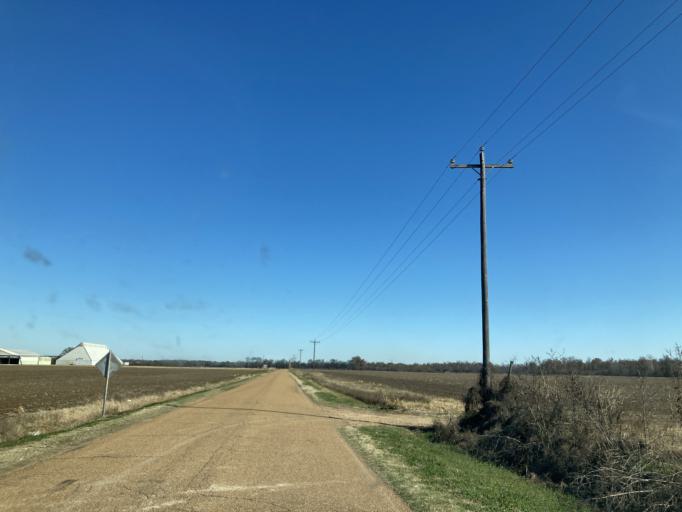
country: US
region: Mississippi
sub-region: Yazoo County
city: Yazoo City
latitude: 32.8995
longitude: -90.4501
